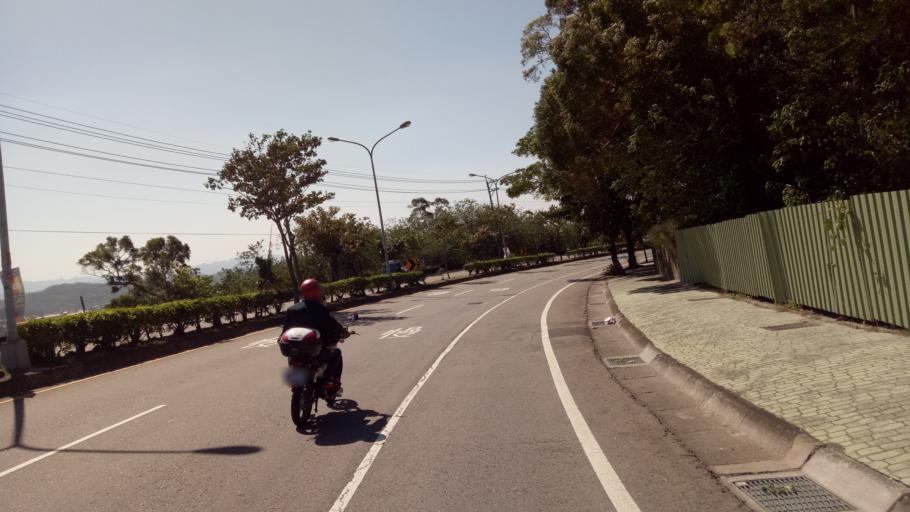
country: TW
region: Taiwan
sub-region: Hsinchu
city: Hsinchu
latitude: 24.7051
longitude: 120.9257
